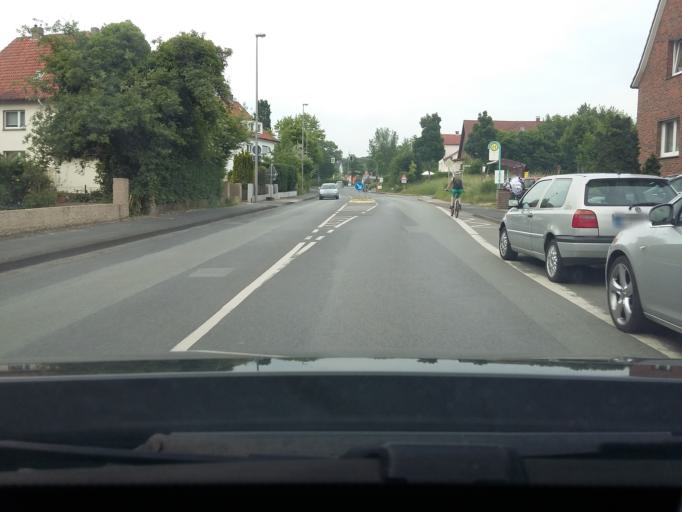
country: DE
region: North Rhine-Westphalia
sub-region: Regierungsbezirk Detmold
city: Bad Salzuflen
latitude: 52.0924
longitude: 8.7613
